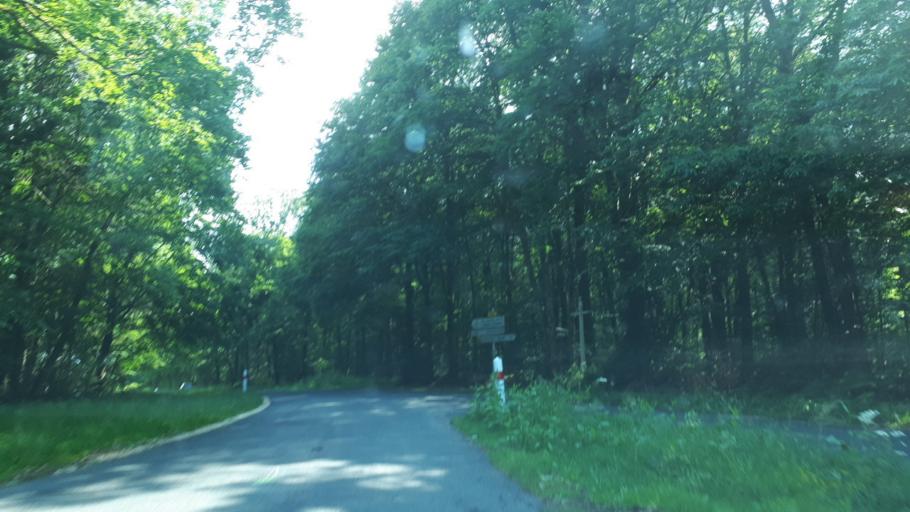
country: FR
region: Centre
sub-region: Departement du Cher
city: Henrichemont
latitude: 47.3955
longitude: 2.5940
